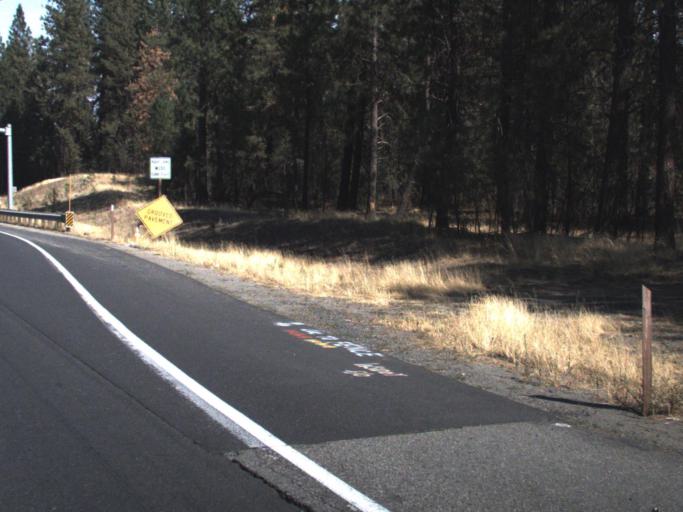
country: US
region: Washington
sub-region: Spokane County
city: Mead
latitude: 47.7706
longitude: -117.3811
